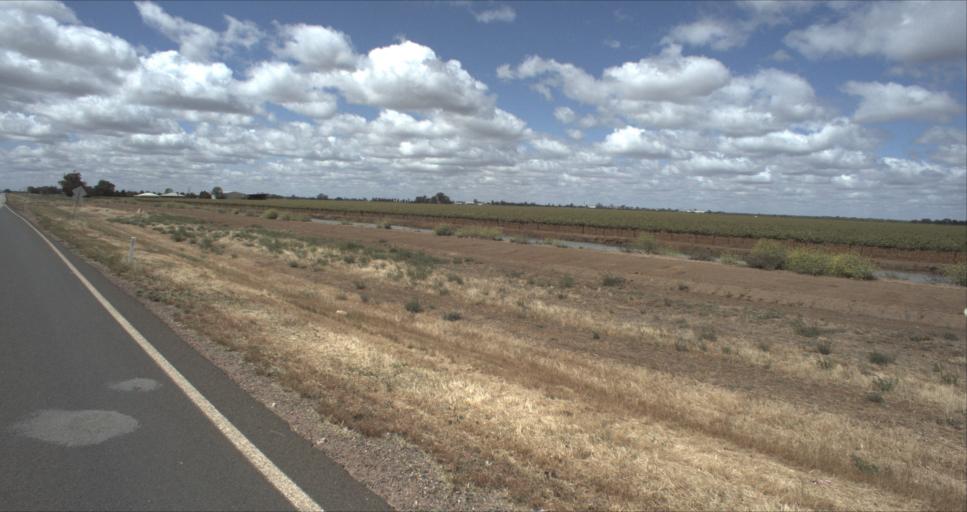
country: AU
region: New South Wales
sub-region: Murrumbidgee Shire
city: Darlington Point
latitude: -34.4948
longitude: 146.1701
